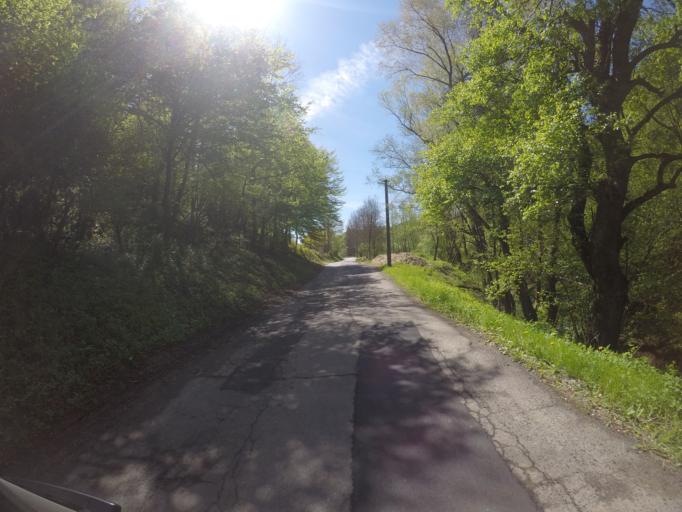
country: SK
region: Banskobystricky
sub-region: Okres Banska Bystrica
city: Banska Bystrica
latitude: 48.7133
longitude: 19.2291
